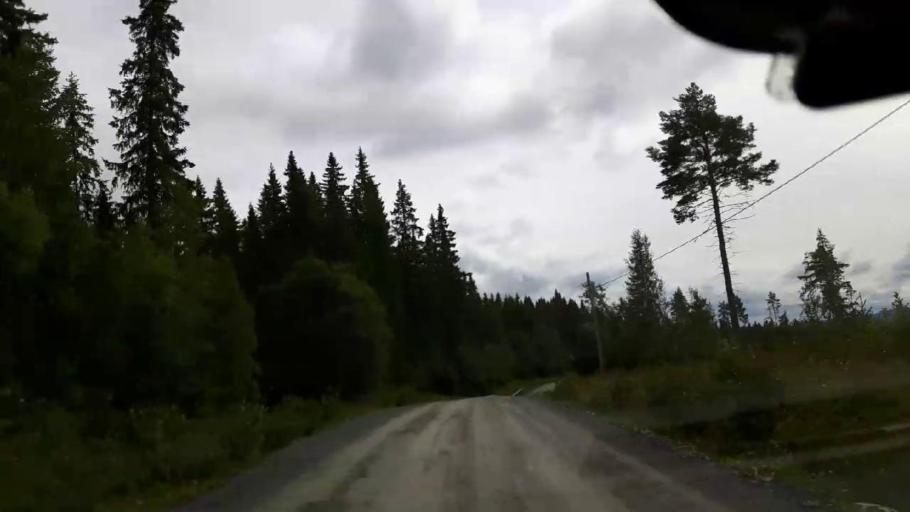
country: SE
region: Jaemtland
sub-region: Krokoms Kommun
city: Valla
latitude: 63.6787
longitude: 13.9307
